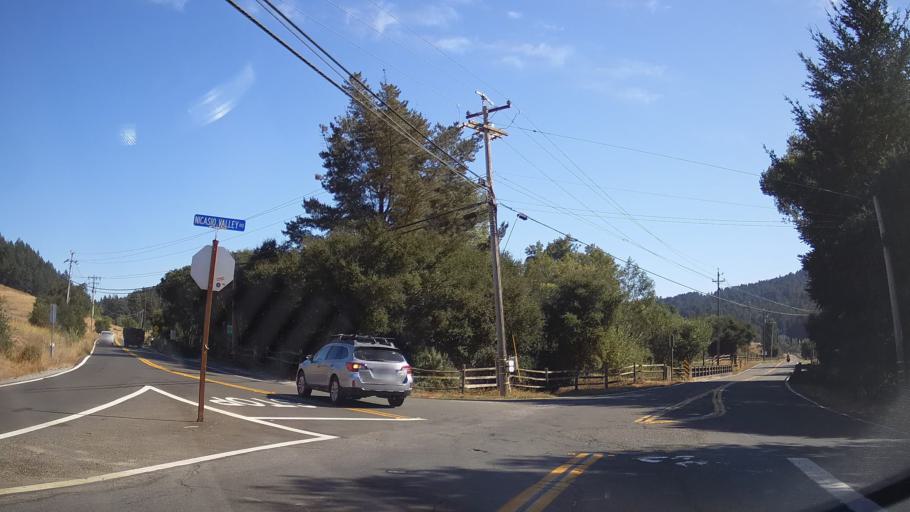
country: US
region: California
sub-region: Marin County
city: Lagunitas-Forest Knolls
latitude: 38.0549
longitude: -122.6932
